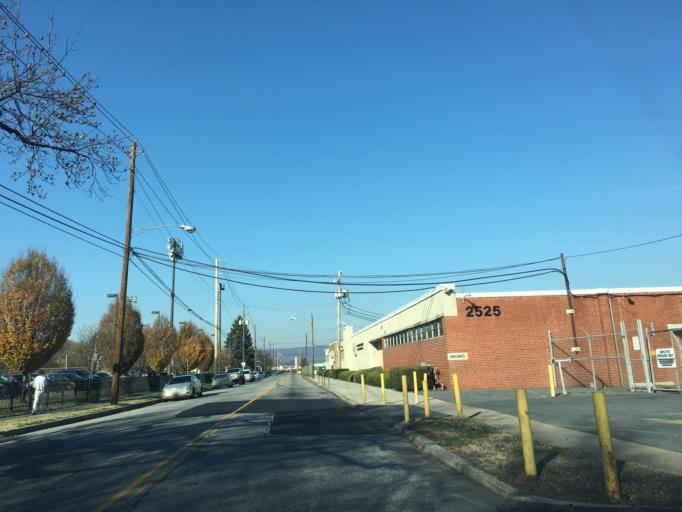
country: US
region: Pennsylvania
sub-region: Dauphin County
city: Harrisburg
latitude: 40.2881
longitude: -76.8907
